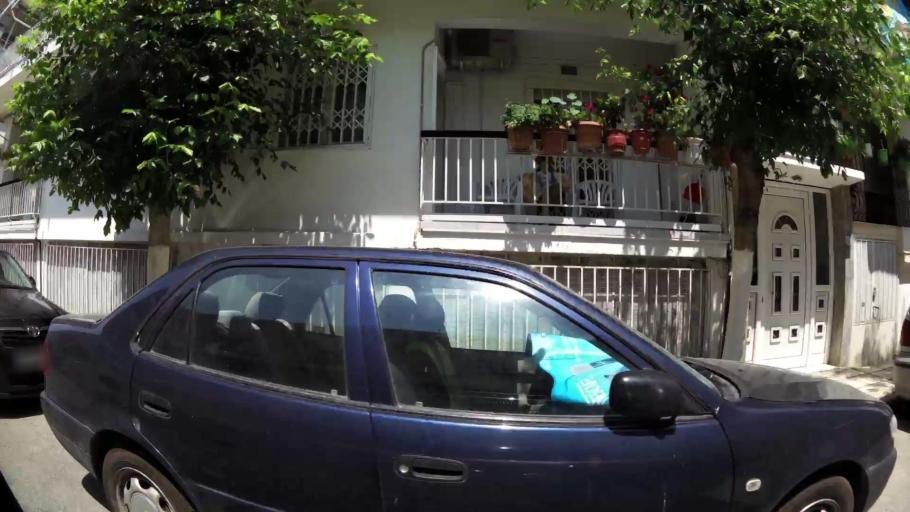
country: GR
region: Central Macedonia
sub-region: Nomos Thessalonikis
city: Ampelokipoi
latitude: 40.6558
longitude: 22.9291
